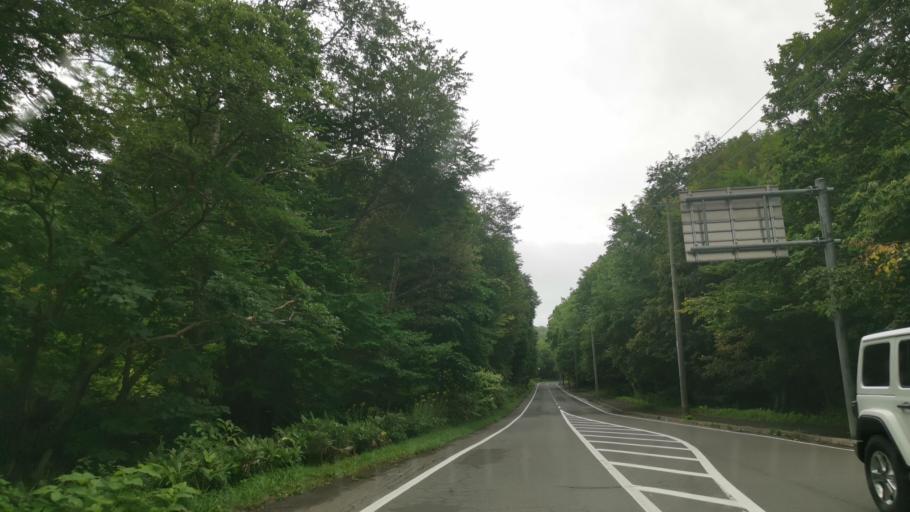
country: JP
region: Hokkaido
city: Sapporo
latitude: 42.9843
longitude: 141.3599
